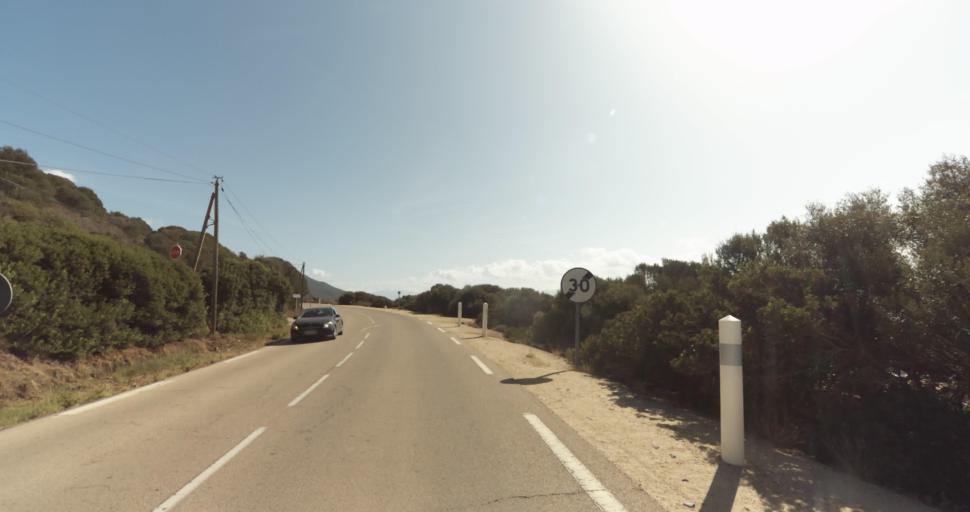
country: FR
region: Corsica
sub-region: Departement de la Corse-du-Sud
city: Ajaccio
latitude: 41.9025
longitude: 8.6234
